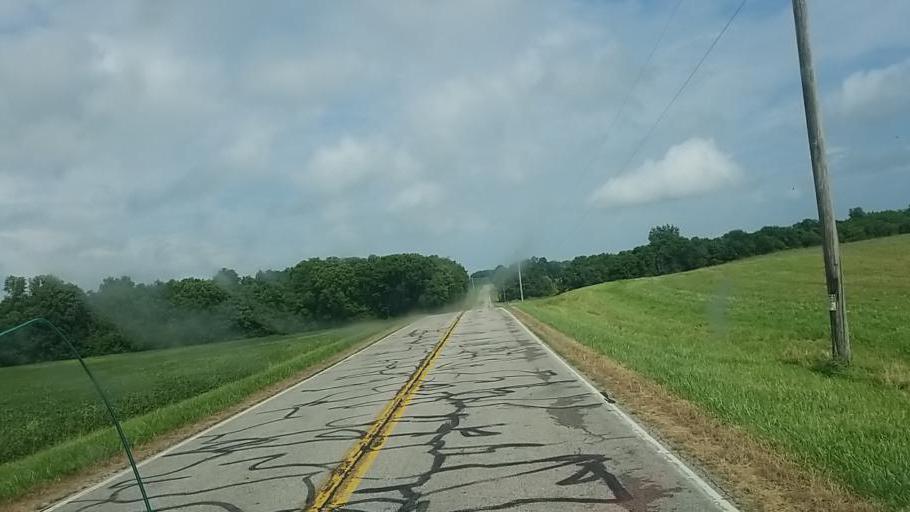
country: US
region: Ohio
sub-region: Logan County
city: West Liberty
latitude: 40.2355
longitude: -83.6758
